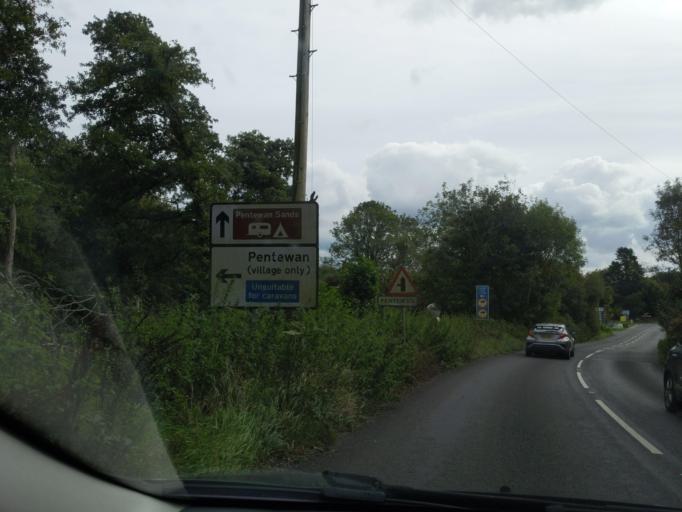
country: GB
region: England
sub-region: Cornwall
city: Mevagissey
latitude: 50.2931
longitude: -4.7865
